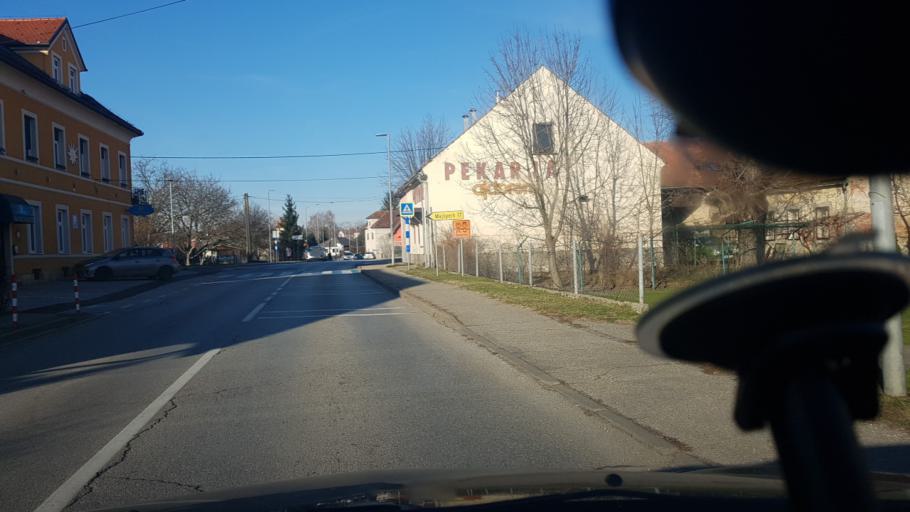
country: SI
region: Ptuj
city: Ptuj
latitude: 46.4136
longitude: 15.8646
